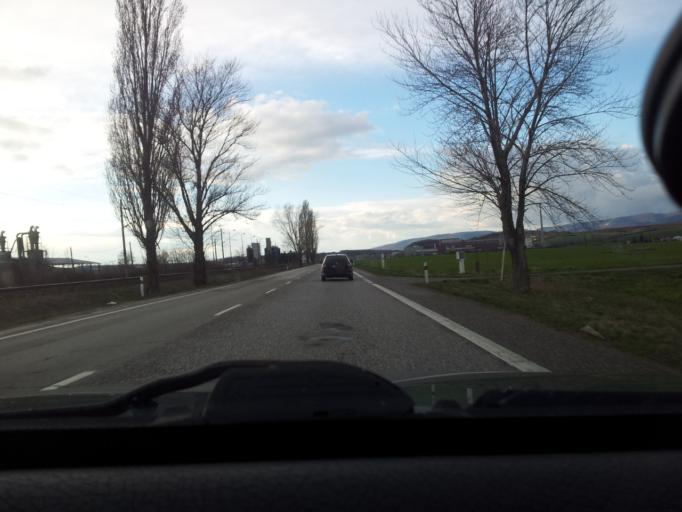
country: SK
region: Nitriansky
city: Tlmace
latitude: 48.2746
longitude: 18.5559
